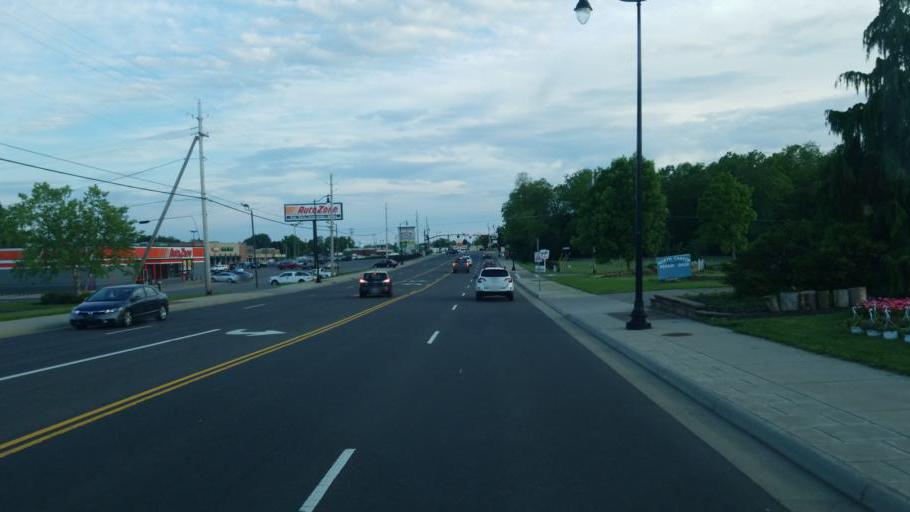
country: US
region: Ohio
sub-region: Stark County
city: North Canton
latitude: 40.8951
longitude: -81.4064
